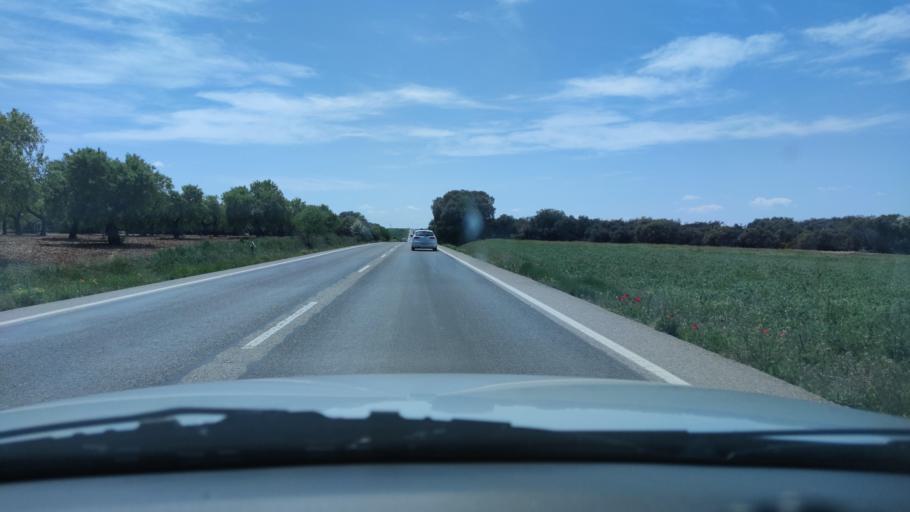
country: ES
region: Catalonia
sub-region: Provincia de Lleida
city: Mont-roig del Camp
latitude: 41.7336
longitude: 1.2135
